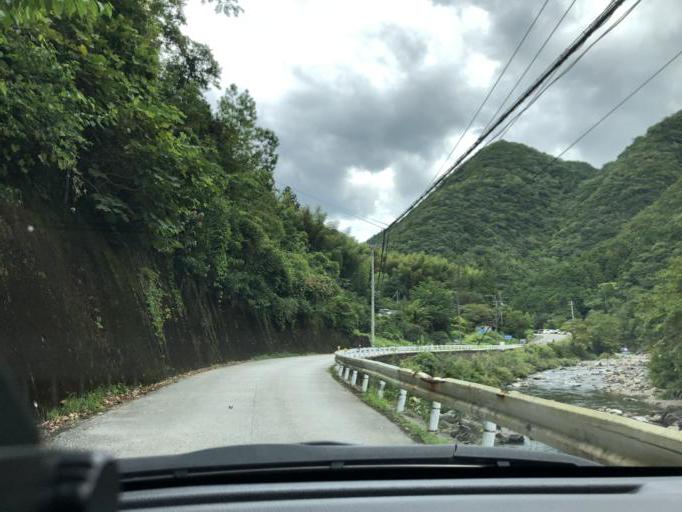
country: JP
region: Kochi
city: Kochi-shi
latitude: 33.6284
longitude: 133.5107
